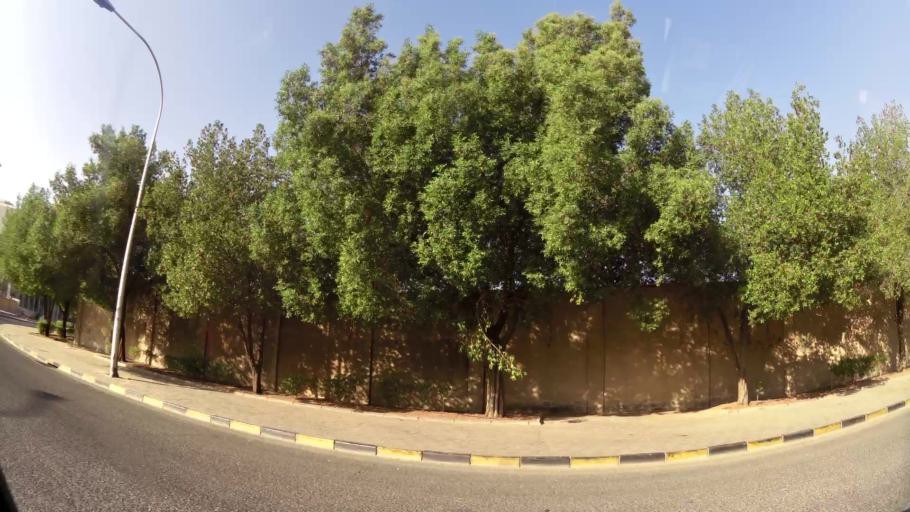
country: KW
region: Al Asimah
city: Kuwait City
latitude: 29.3714
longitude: 47.9880
